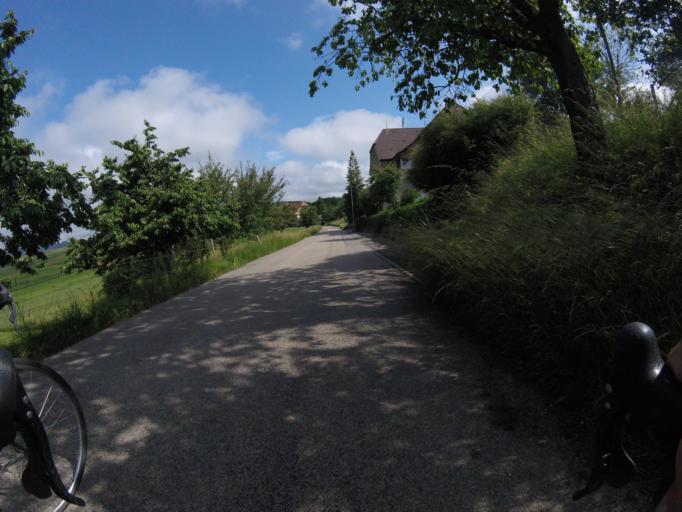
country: CH
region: Bern
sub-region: Bern-Mittelland District
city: Vechigen
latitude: 46.9436
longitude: 7.5850
